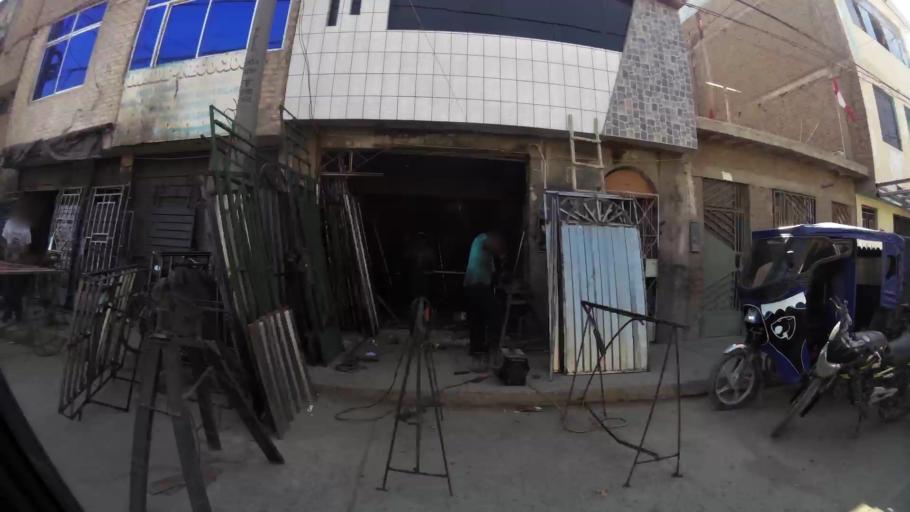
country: PE
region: Lambayeque
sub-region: Provincia de Chiclayo
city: Santa Rosa
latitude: -6.7630
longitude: -79.8402
